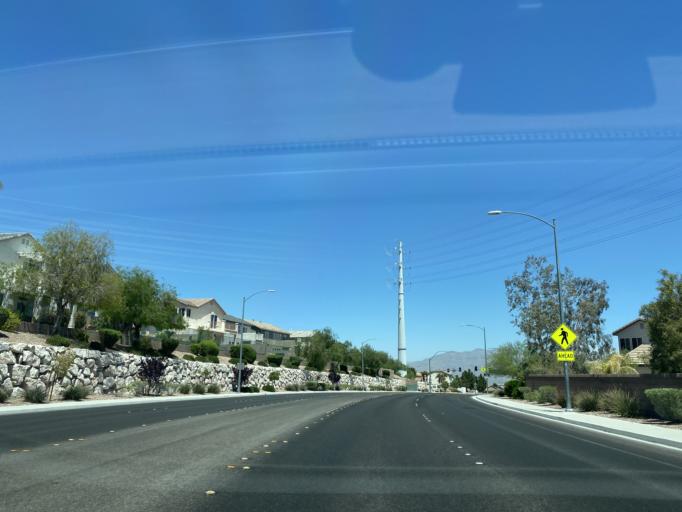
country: US
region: Nevada
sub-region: Clark County
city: Summerlin South
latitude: 36.2384
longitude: -115.3303
